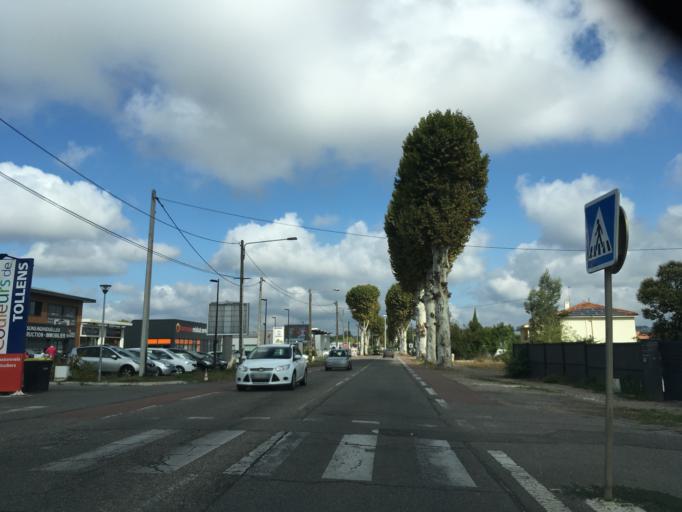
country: FR
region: Aquitaine
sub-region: Departement du Lot-et-Garonne
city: Agen
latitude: 44.1814
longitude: 0.6234
